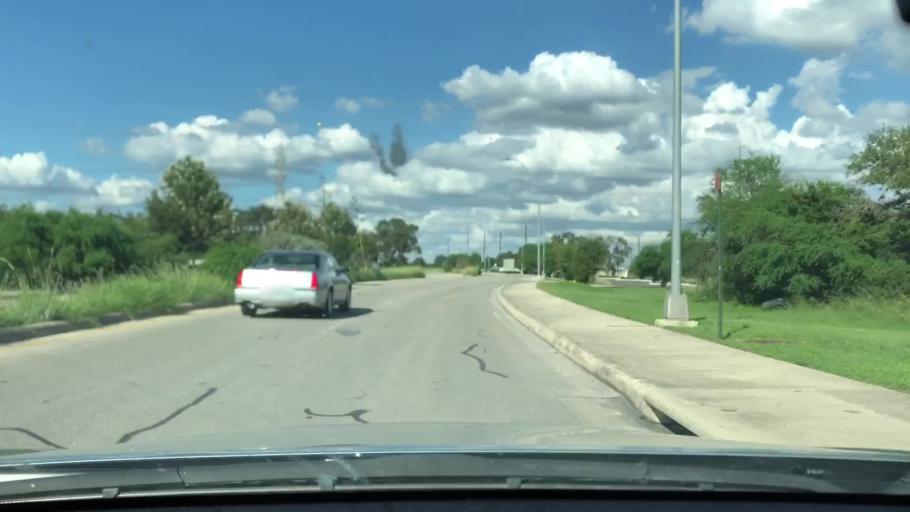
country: US
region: Texas
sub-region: Bexar County
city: Hollywood Park
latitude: 29.6151
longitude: -98.4780
